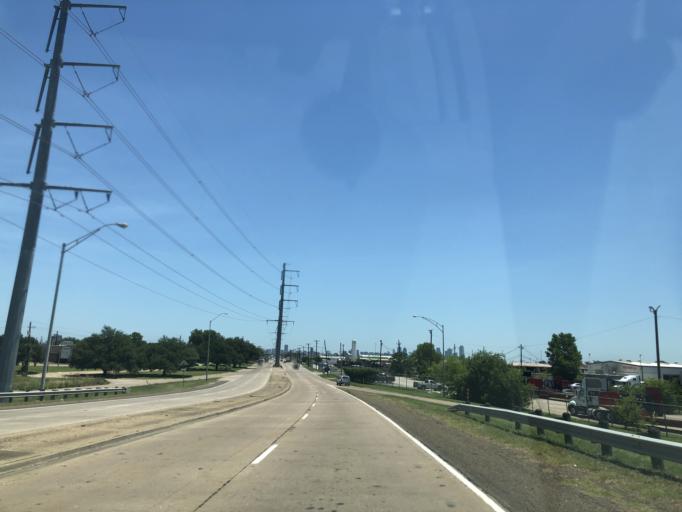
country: US
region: Texas
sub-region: Dallas County
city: Irving
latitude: 32.8083
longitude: -96.9002
